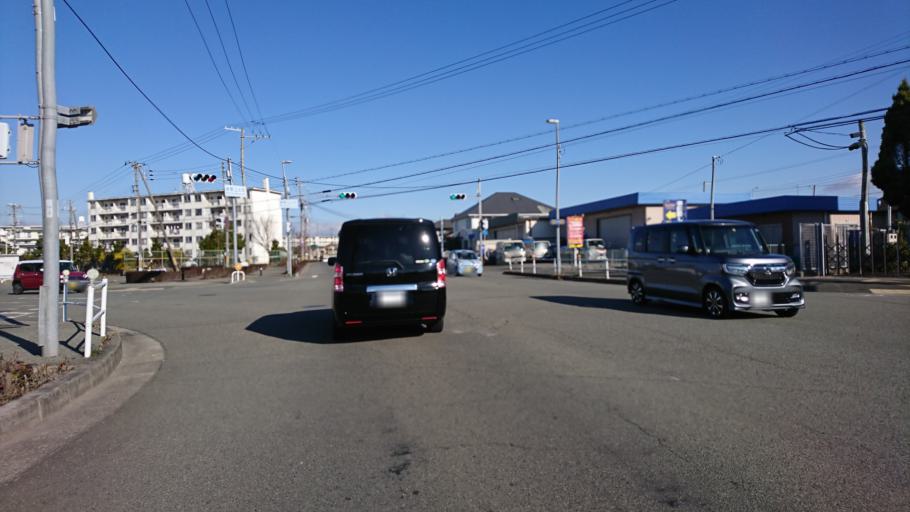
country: JP
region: Hyogo
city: Kakogawacho-honmachi
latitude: 34.7382
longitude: 134.8421
